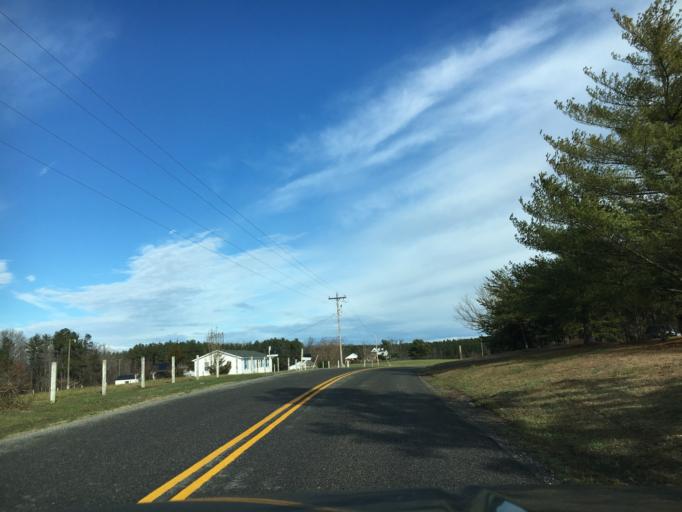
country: US
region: Virginia
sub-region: Nottoway County
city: Crewe
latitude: 37.2855
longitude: -78.2033
